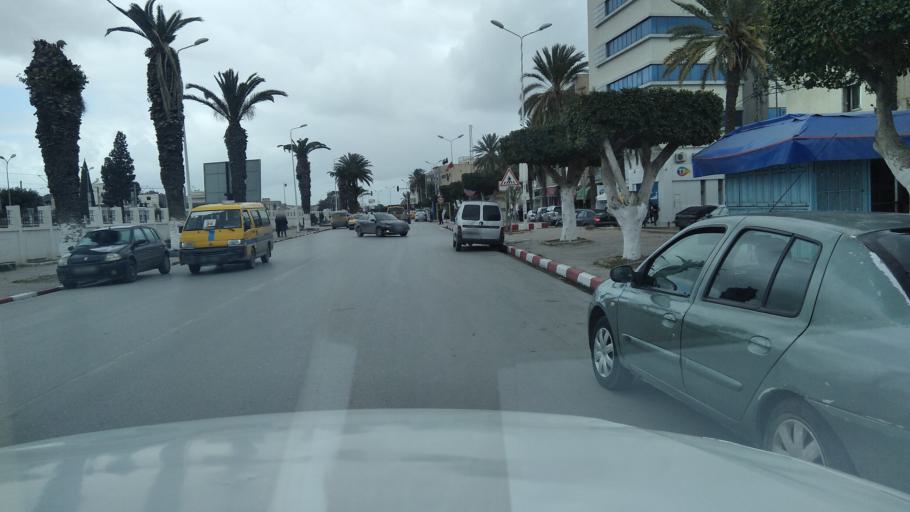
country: TN
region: Bin 'Arus
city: Ben Arous
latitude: 36.7552
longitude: 10.2212
